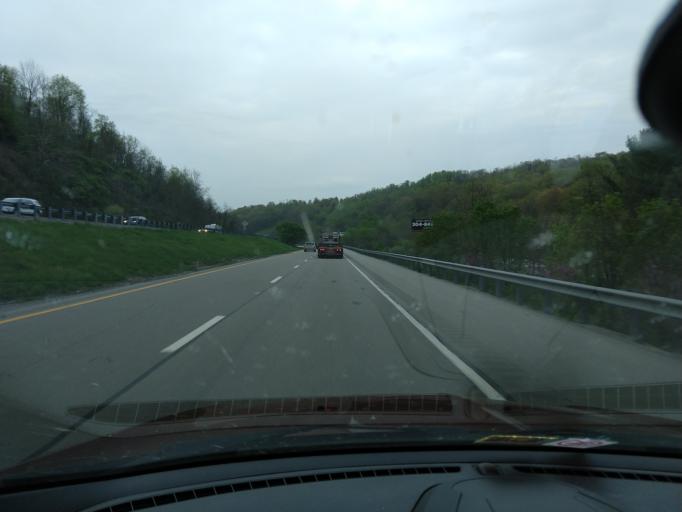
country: US
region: West Virginia
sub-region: Harrison County
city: Stonewood
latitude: 39.1490
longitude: -80.3614
